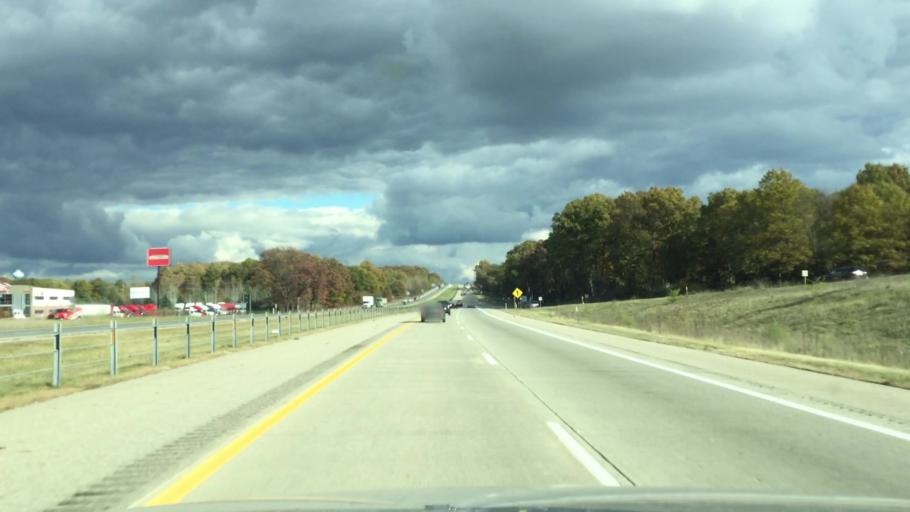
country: US
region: Michigan
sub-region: Van Buren County
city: Mattawan
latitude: 42.2228
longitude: -85.7847
